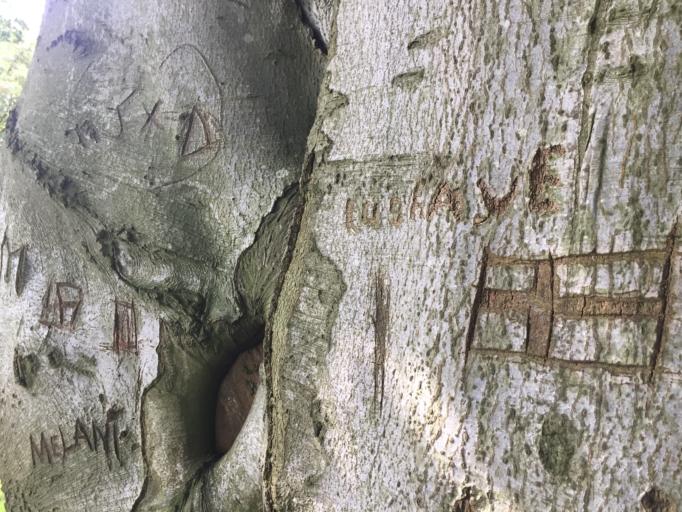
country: DK
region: South Denmark
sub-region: Assens Kommune
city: Vissenbjerg
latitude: 55.3389
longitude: 10.1164
